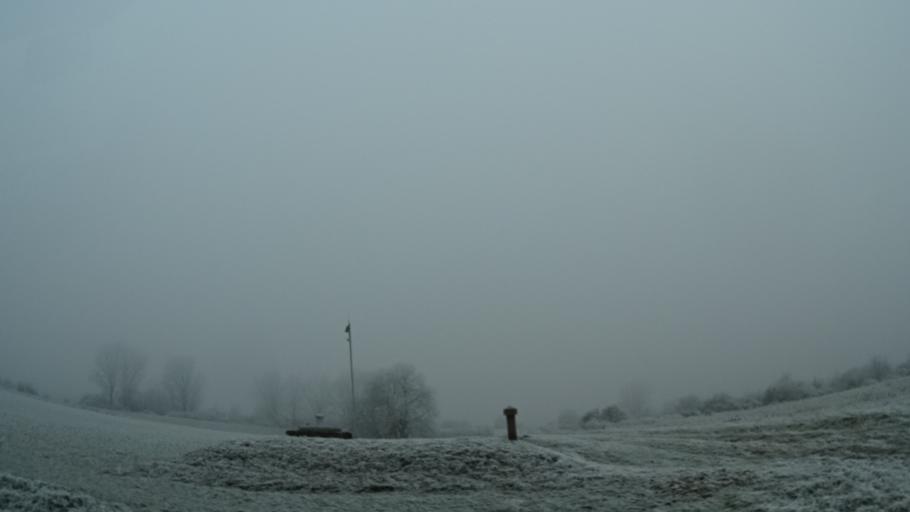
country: DE
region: Bavaria
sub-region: Regierungsbezirk Unterfranken
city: Donnersdorf
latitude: 49.9622
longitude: 10.4230
